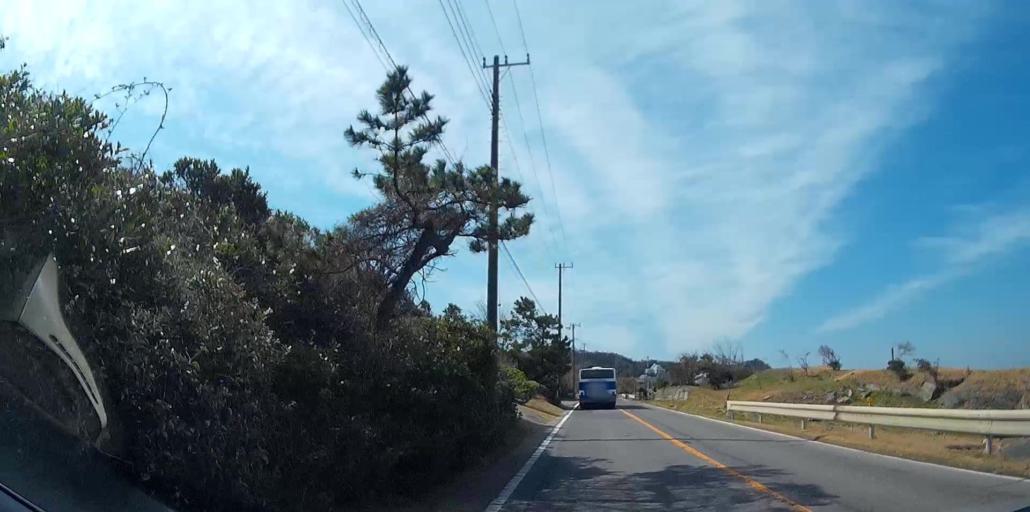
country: JP
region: Chiba
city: Tateyama
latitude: 34.9736
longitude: 139.7969
